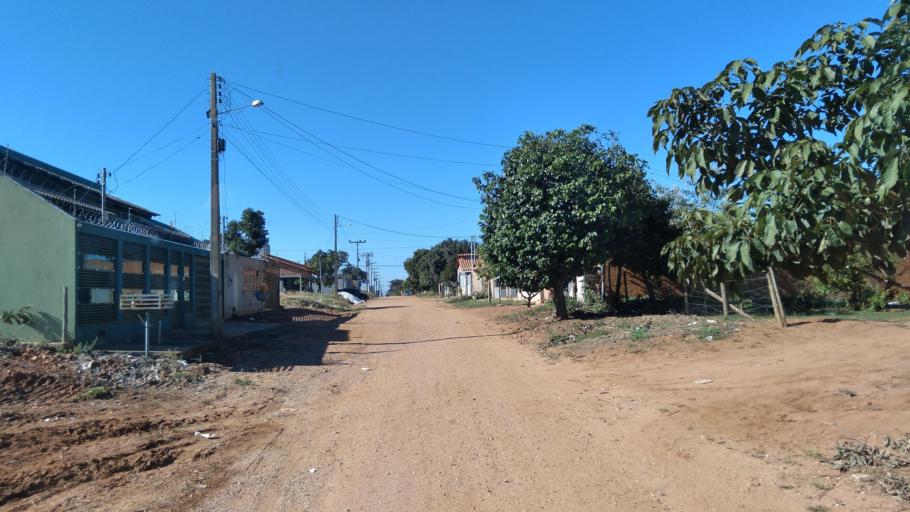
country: BR
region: Goias
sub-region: Mineiros
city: Mineiros
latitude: -17.5889
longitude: -52.5574
